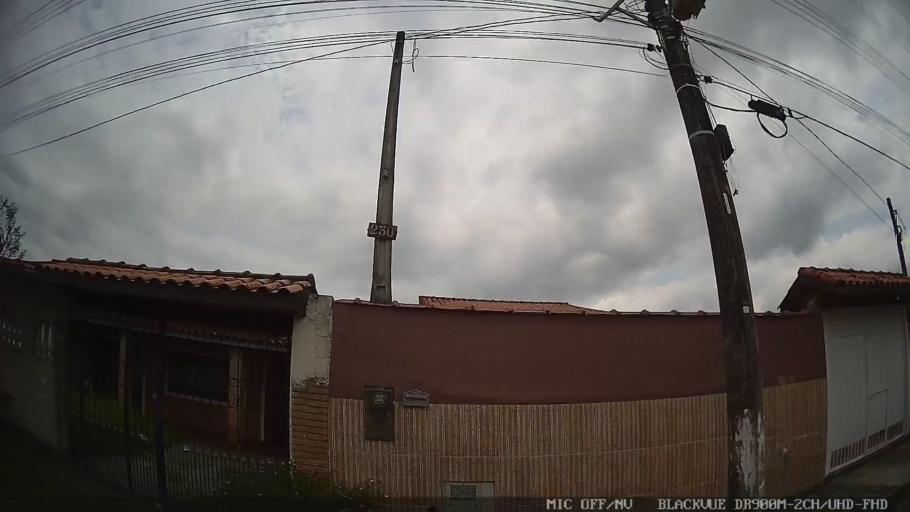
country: BR
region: Sao Paulo
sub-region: Caraguatatuba
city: Caraguatatuba
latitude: -23.6736
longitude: -45.4398
